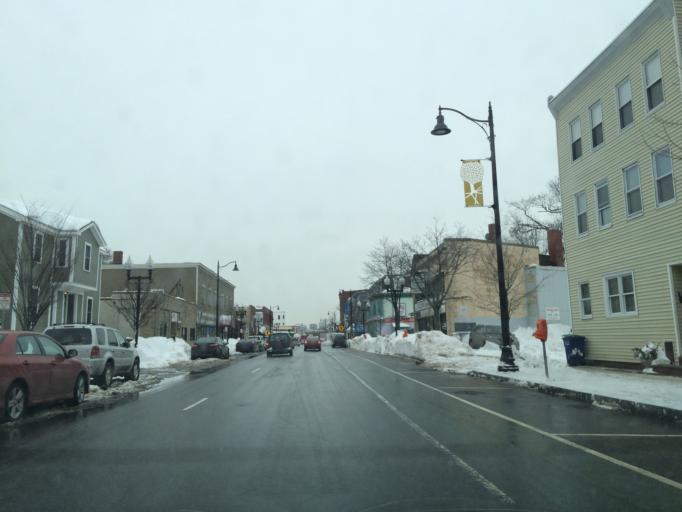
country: US
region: Massachusetts
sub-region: Middlesex County
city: Somerville
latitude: 42.3810
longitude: -71.0989
